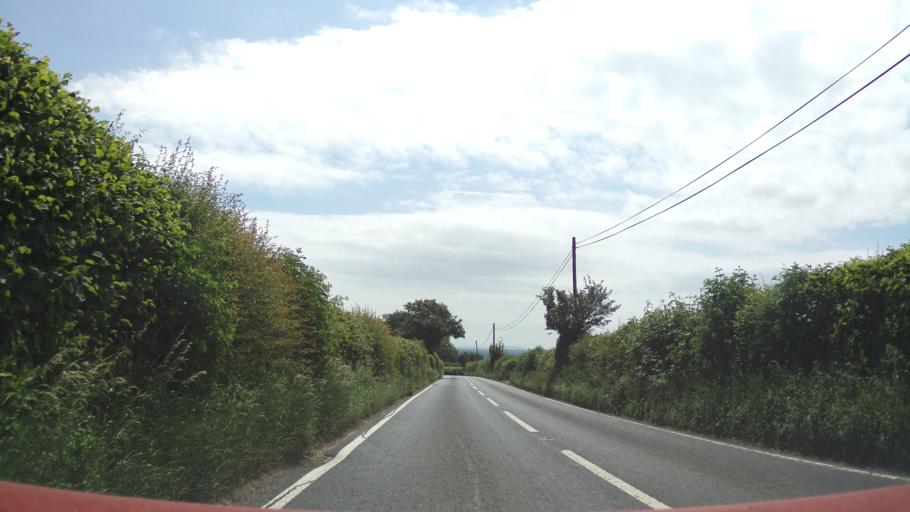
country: GB
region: England
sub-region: Somerset
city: Wincanton
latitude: 51.0569
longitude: -2.4511
